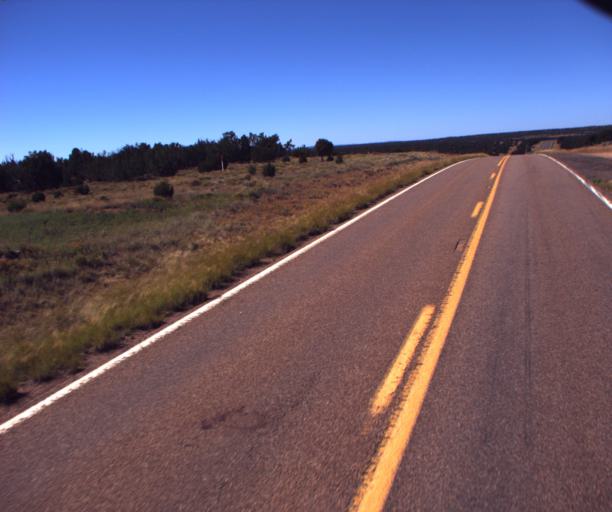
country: US
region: Arizona
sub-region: Navajo County
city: Heber-Overgaard
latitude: 34.4583
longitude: -110.4376
